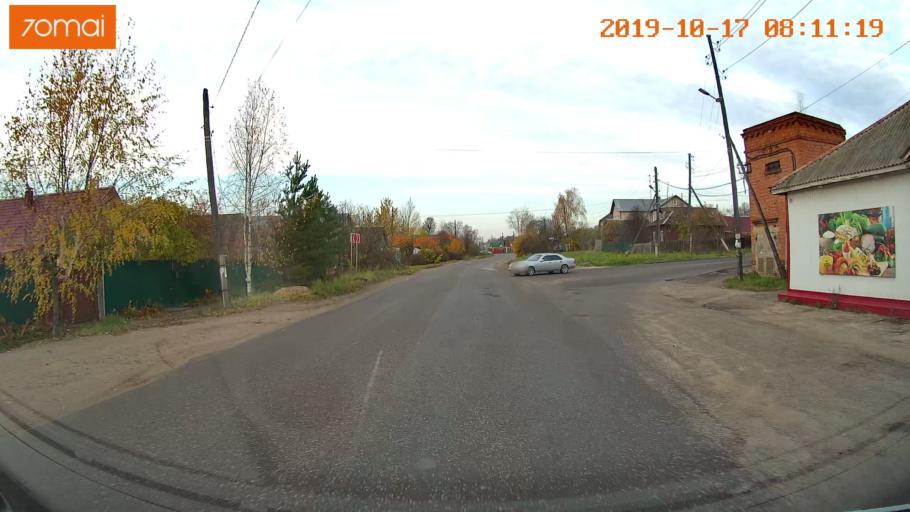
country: RU
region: Vladimir
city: Kol'chugino
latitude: 56.3034
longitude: 39.3715
